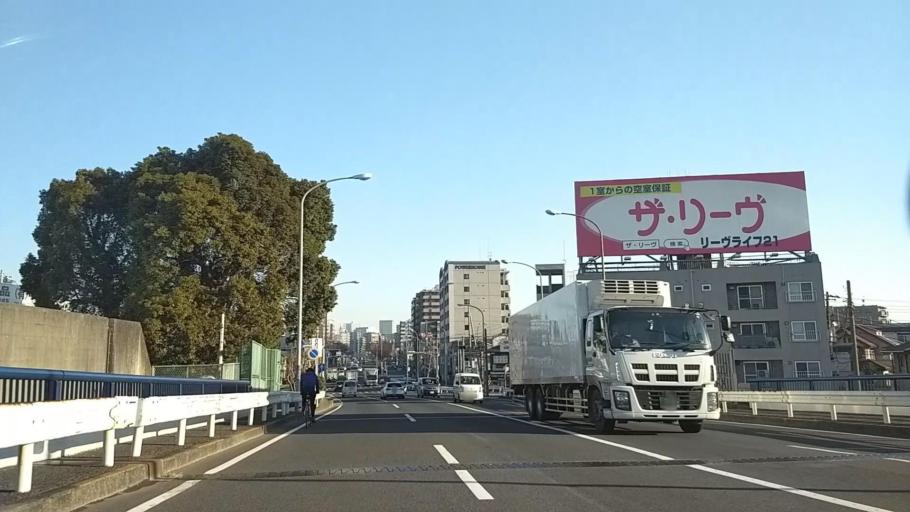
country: JP
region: Kanagawa
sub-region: Kawasaki-shi
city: Kawasaki
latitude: 35.5132
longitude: 139.6856
